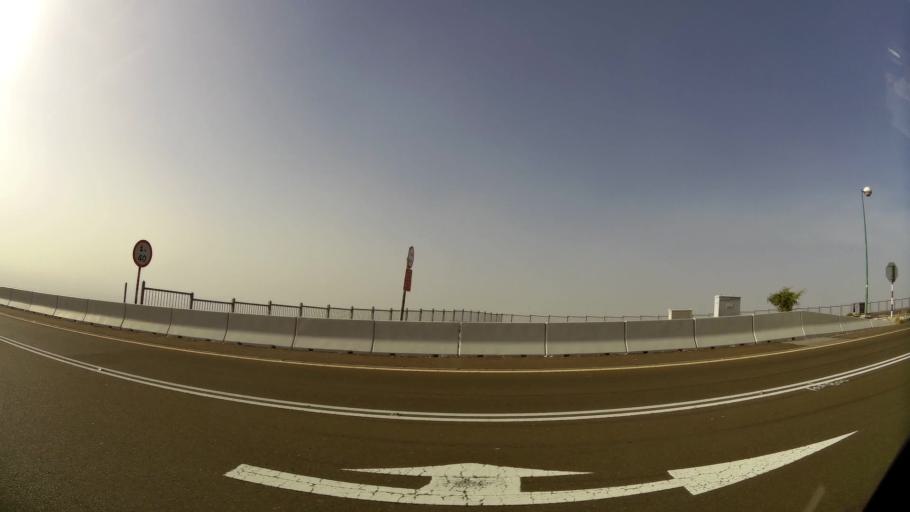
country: AE
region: Abu Dhabi
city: Al Ain
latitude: 24.0833
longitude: 55.7671
